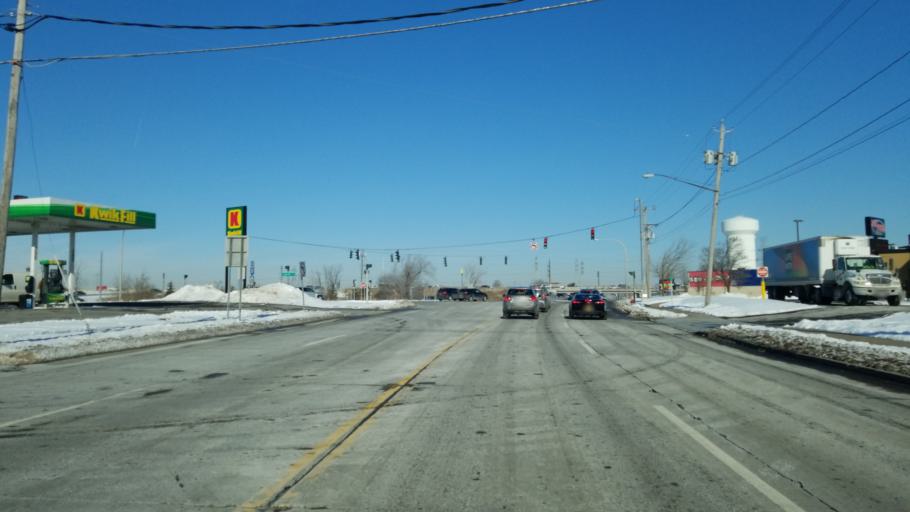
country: US
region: New York
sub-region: Erie County
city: Tonawanda
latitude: 42.9978
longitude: -78.8512
